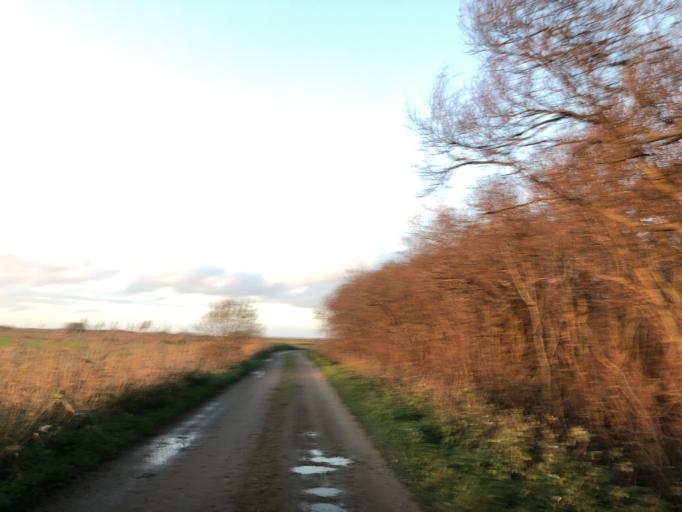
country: DK
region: Central Jutland
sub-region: Holstebro Kommune
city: Ulfborg
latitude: 56.2888
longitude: 8.2925
